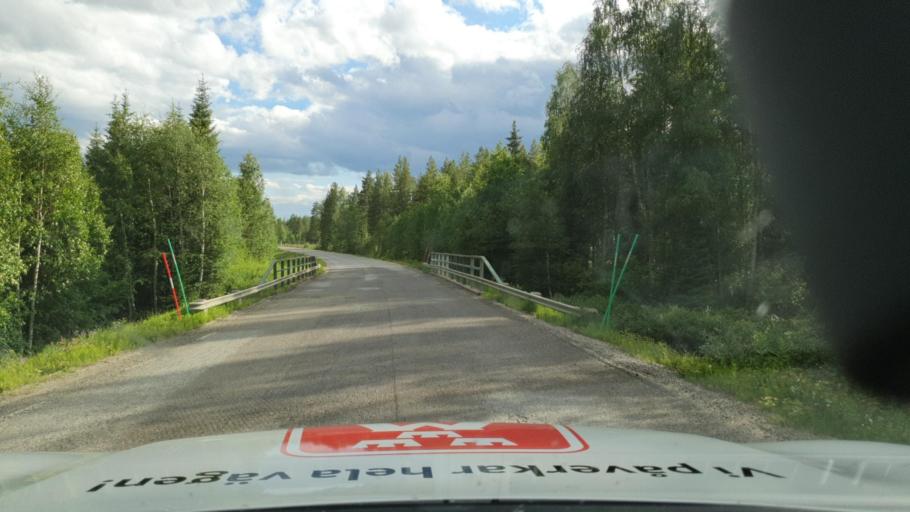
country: SE
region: Vaesterbotten
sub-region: Vindelns Kommun
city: Vindeln
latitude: 64.3803
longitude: 19.6610
